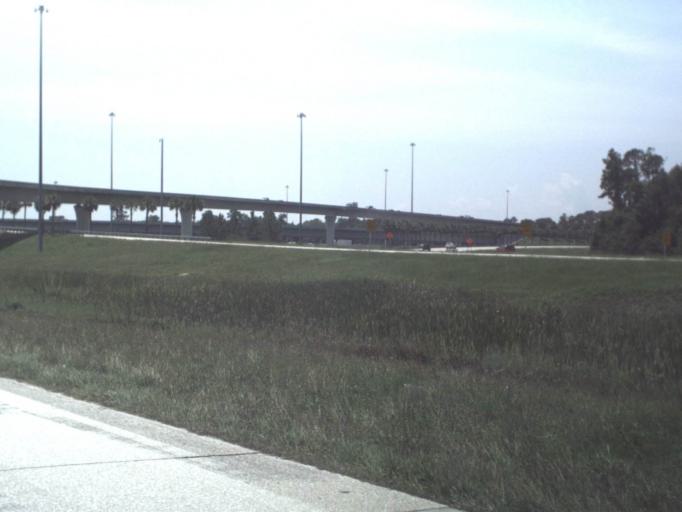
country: US
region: Florida
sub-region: Saint Johns County
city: Fruit Cove
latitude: 30.1716
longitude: -81.5576
